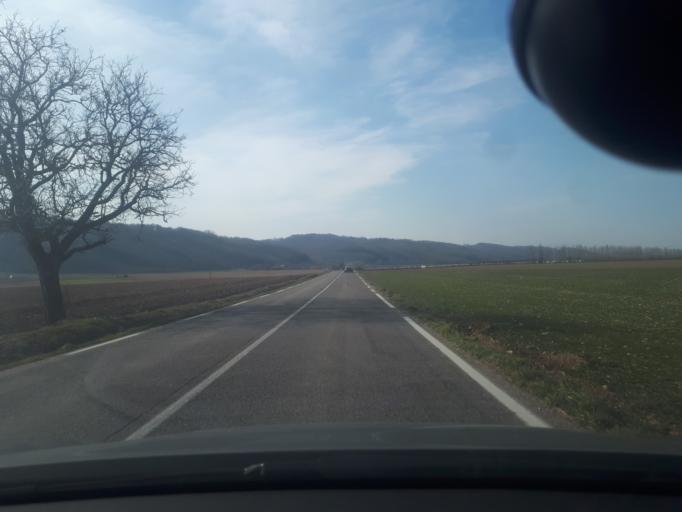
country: FR
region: Rhone-Alpes
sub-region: Departement de l'Isere
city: La Cote-Saint-Andre
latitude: 45.4254
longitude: 5.2722
